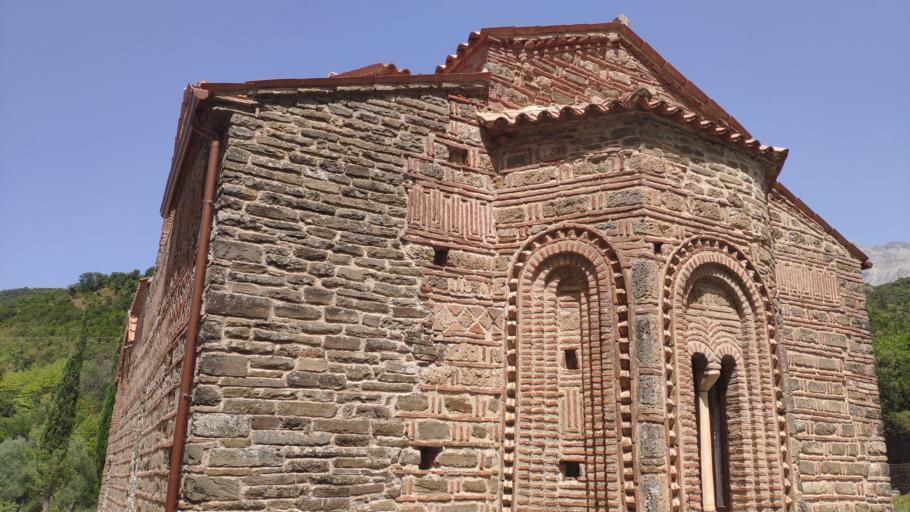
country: GR
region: Epirus
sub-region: Nomos Artas
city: Voulgareli
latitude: 39.3545
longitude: 21.1862
